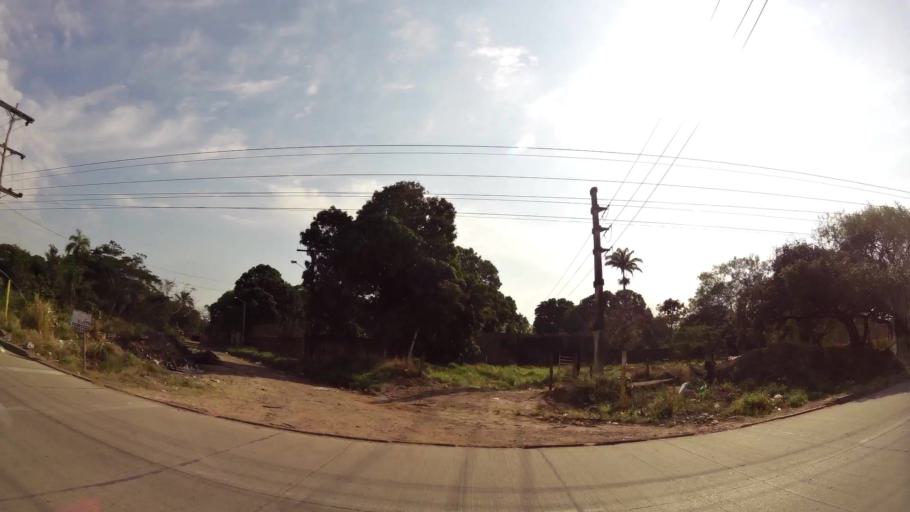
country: BO
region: Santa Cruz
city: Santa Cruz de la Sierra
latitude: -17.7341
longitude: -63.1619
